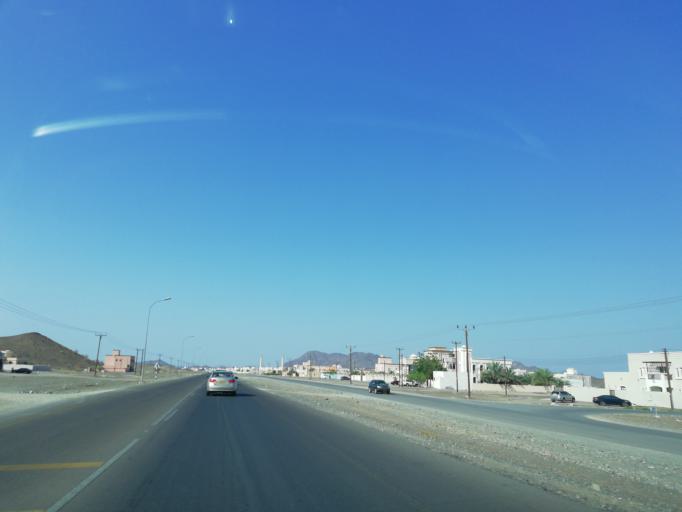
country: OM
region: Ash Sharqiyah
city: Ibra'
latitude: 22.7899
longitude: 58.1470
